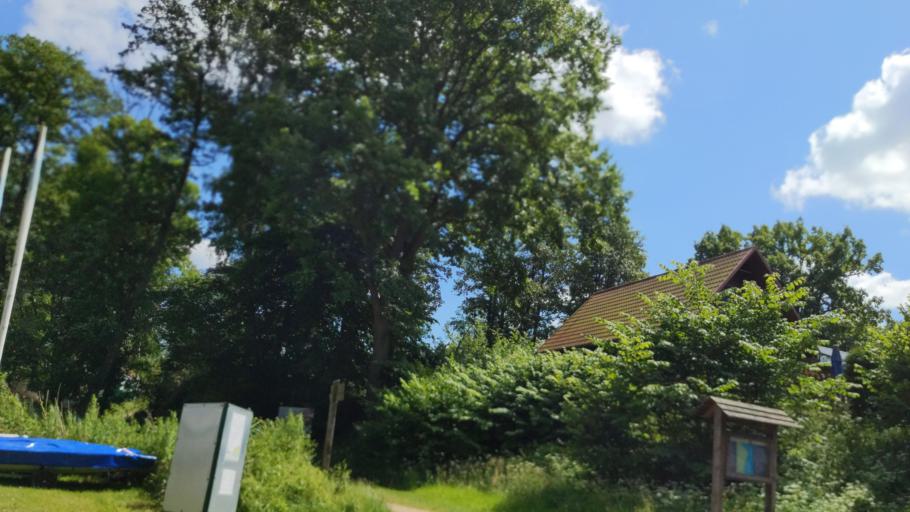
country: DE
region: Schleswig-Holstein
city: Buchholz
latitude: 53.7391
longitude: 10.7406
